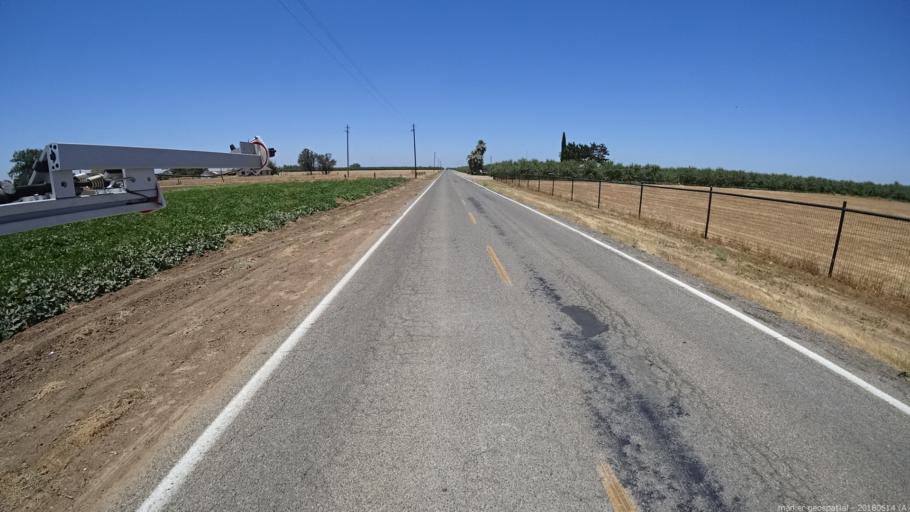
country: US
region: California
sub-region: Madera County
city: Fairmead
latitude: 37.0183
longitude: -120.2061
